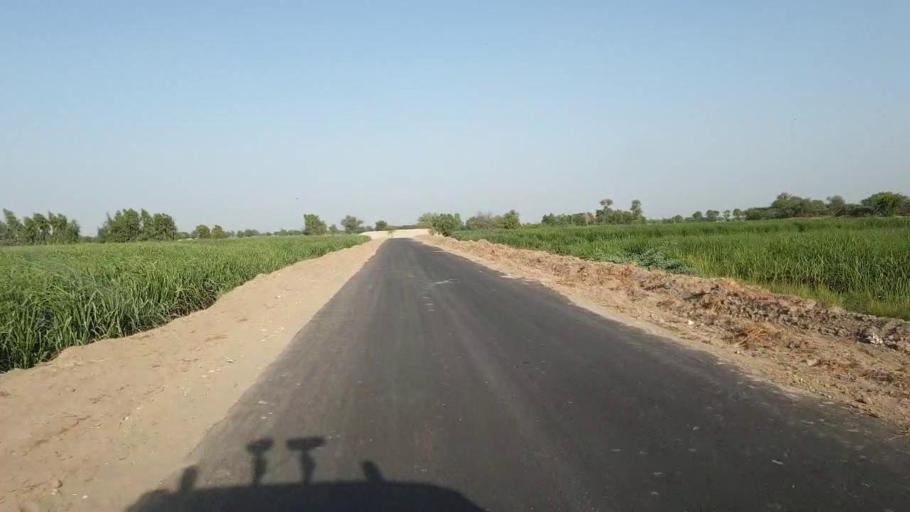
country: PK
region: Sindh
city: Jam Sahib
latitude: 26.3482
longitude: 68.5671
